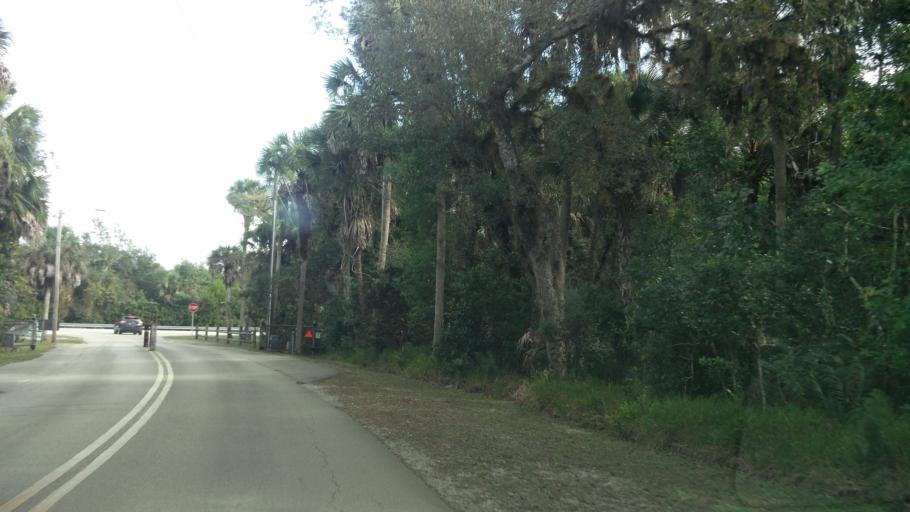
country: US
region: Florida
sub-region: Collier County
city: Lely Resort
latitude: 25.9917
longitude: -81.5905
